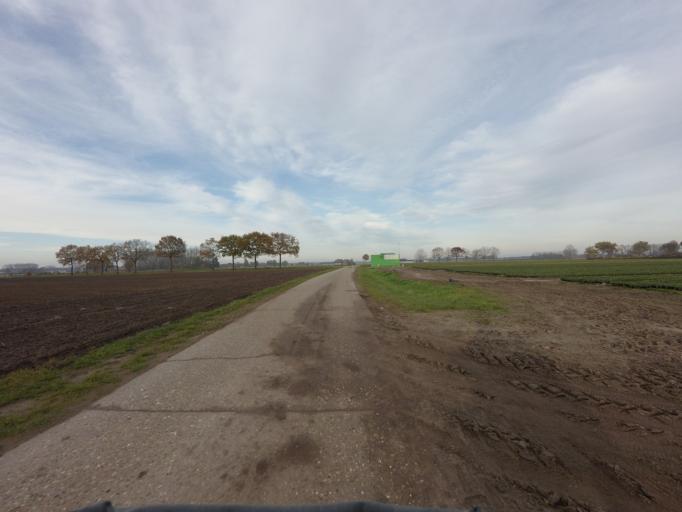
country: BE
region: Flanders
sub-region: Provincie Antwerpen
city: Hoogstraten
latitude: 51.4599
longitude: 4.7678
